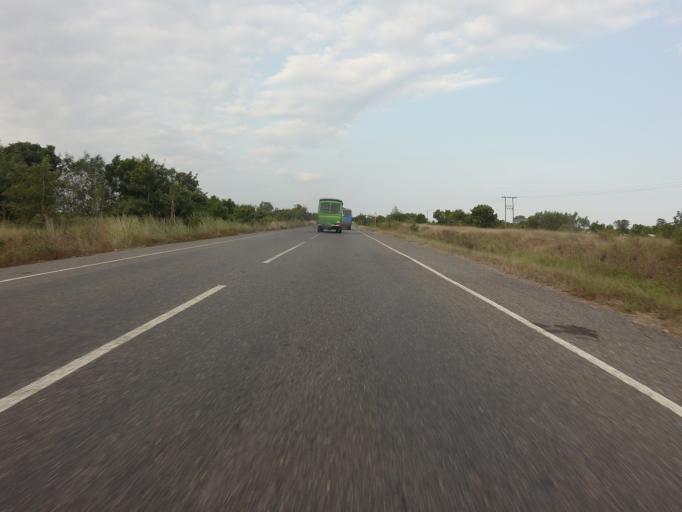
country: GH
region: Volta
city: Anloga
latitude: 6.0903
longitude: 0.5262
